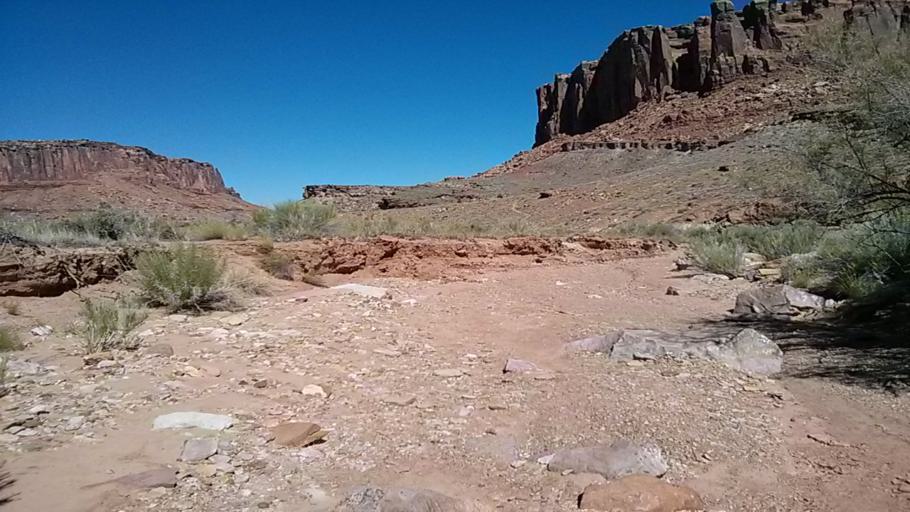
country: US
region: Utah
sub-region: Grand County
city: Moab
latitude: 38.4432
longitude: -109.9509
